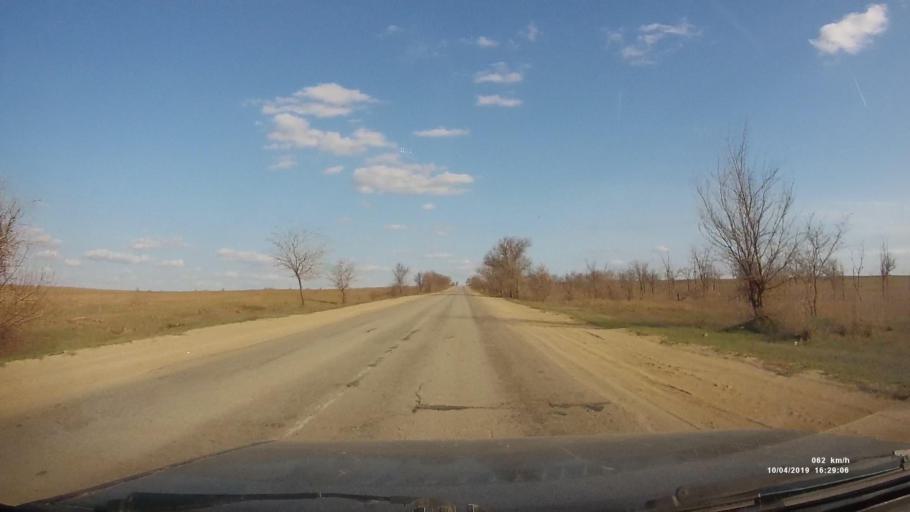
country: RU
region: Rostov
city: Staraya Stanitsa
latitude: 48.2703
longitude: 40.3513
